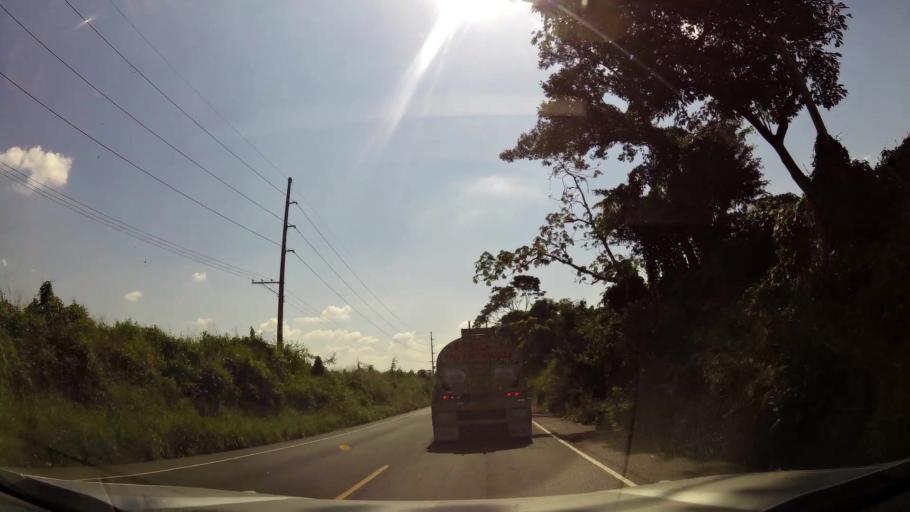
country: GT
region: Suchitepeque
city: Mazatenango
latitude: 14.5451
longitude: -91.5218
